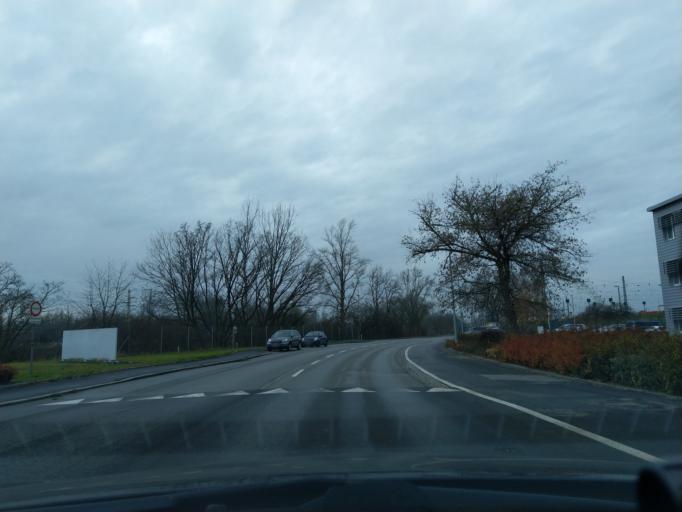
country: AT
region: Upper Austria
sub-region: Politischer Bezirk Urfahr-Umgebung
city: Steyregg
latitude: 48.2617
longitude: 14.3364
